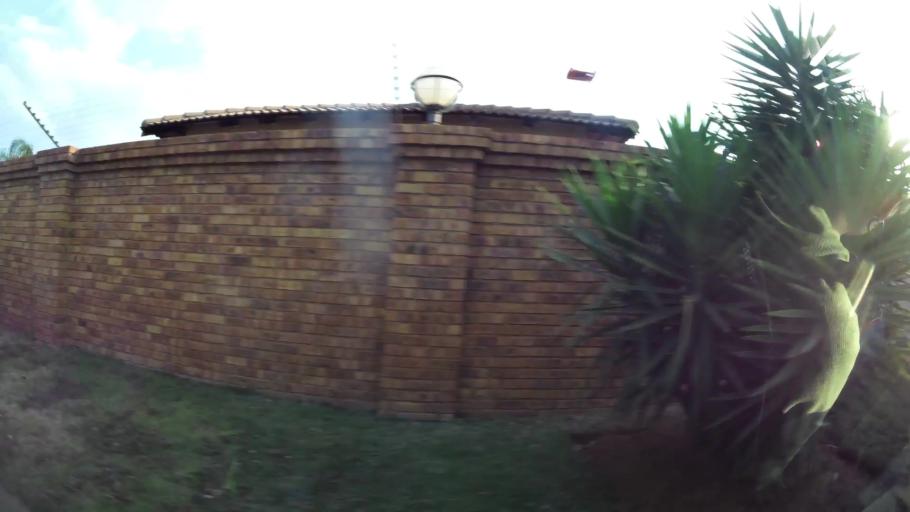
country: ZA
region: Gauteng
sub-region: Ekurhuleni Metropolitan Municipality
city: Benoni
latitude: -26.1241
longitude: 28.2902
